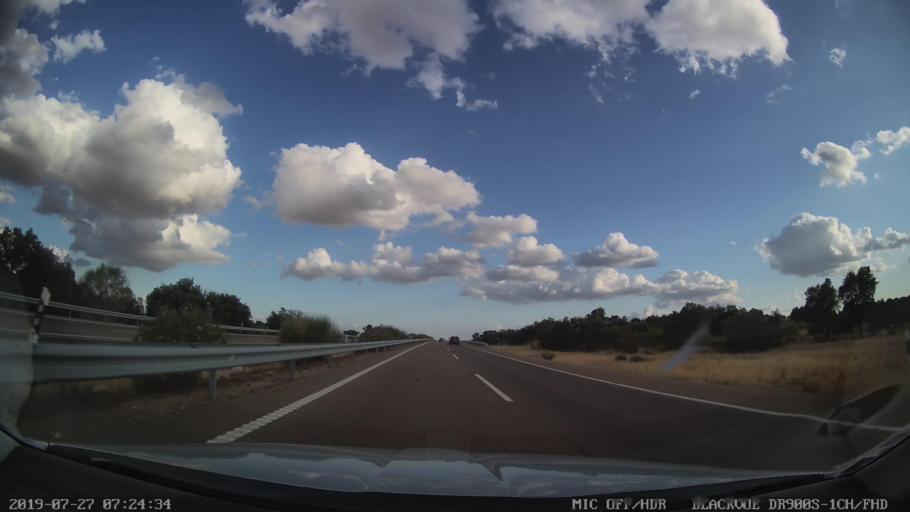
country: ES
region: Extremadura
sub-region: Provincia de Caceres
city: Puerto de Santa Cruz
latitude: 39.2948
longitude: -5.8554
